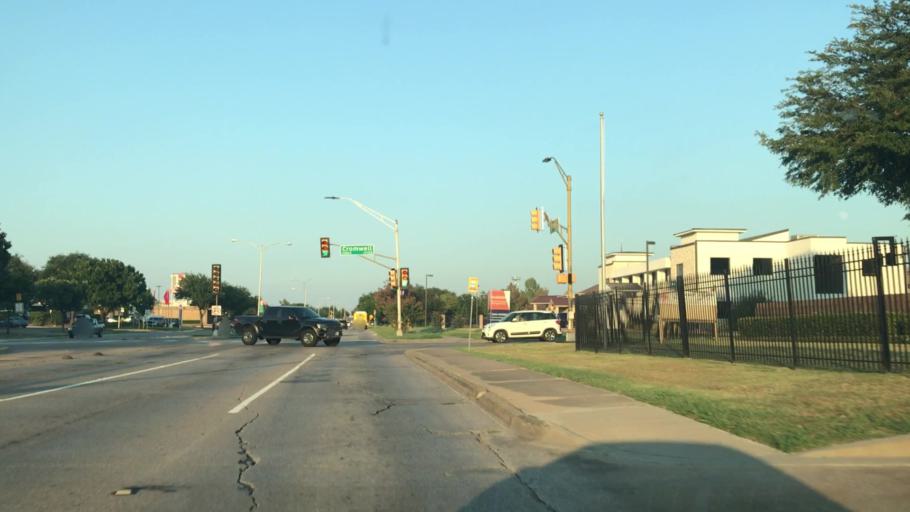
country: US
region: Texas
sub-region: Dallas County
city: Farmers Branch
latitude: 32.9095
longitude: -96.8644
